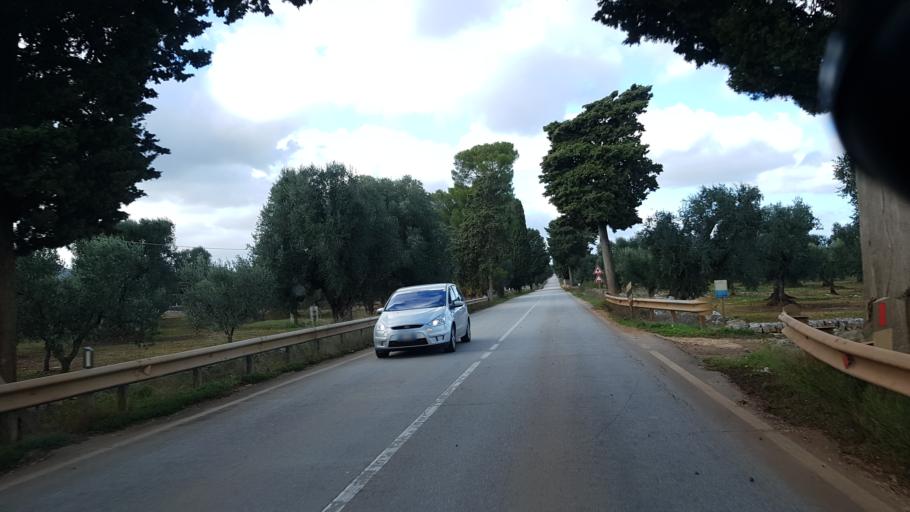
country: IT
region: Apulia
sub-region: Provincia di Brindisi
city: Montalbano
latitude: 40.7621
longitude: 17.5255
